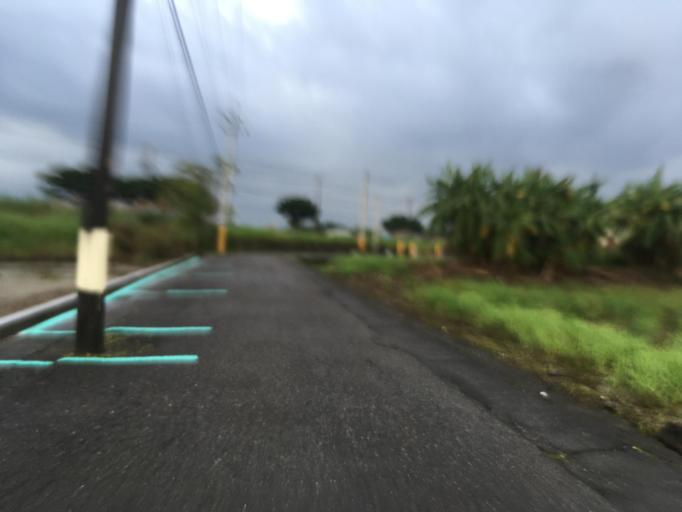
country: TW
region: Taiwan
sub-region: Yilan
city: Yilan
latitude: 24.8280
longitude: 121.8007
